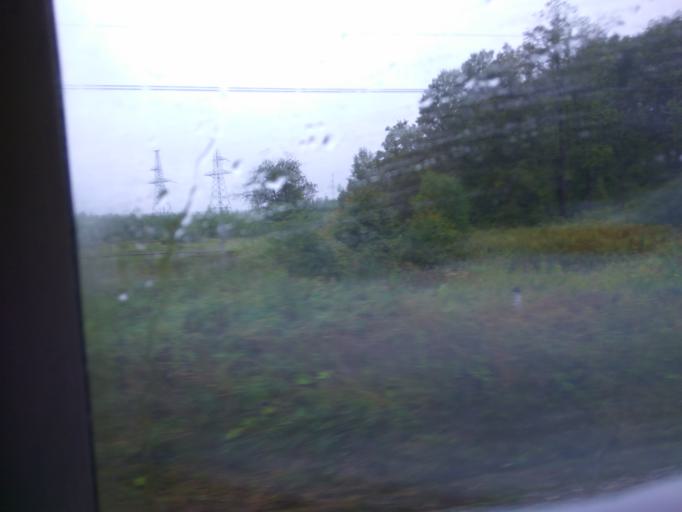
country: RU
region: Moskovskaya
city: Zhilevo
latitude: 55.0181
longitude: 38.0144
